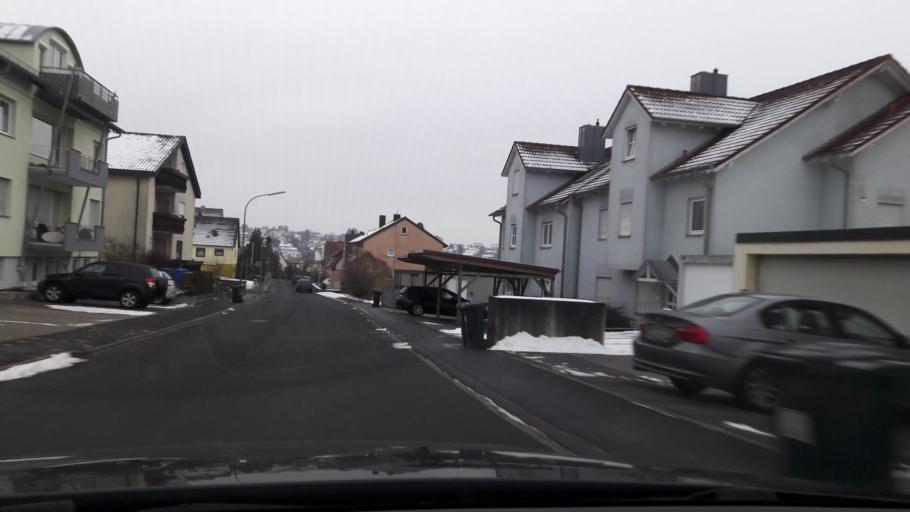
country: DE
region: Bavaria
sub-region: Regierungsbezirk Unterfranken
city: Hochberg
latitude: 49.7839
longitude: 9.8680
